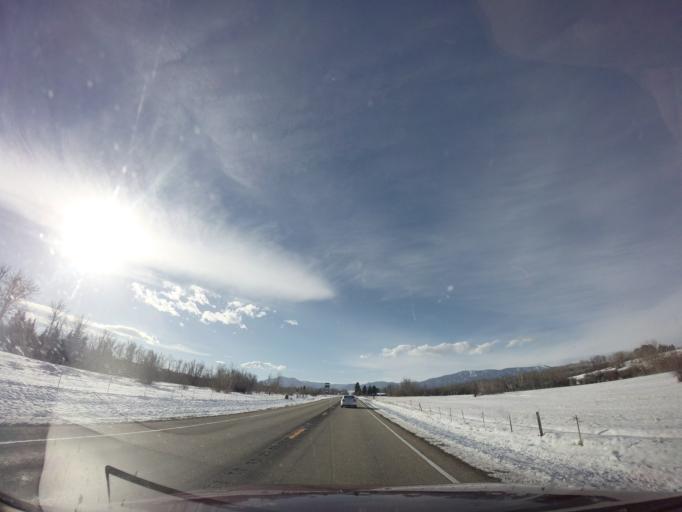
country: US
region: Montana
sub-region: Carbon County
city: Red Lodge
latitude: 45.2808
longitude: -109.2152
